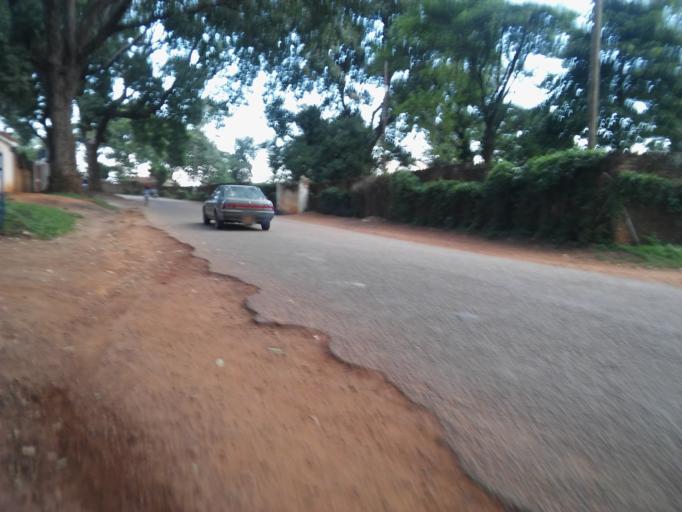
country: UG
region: Eastern Region
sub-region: Mbale District
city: Mbale
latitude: 1.0658
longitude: 34.1980
